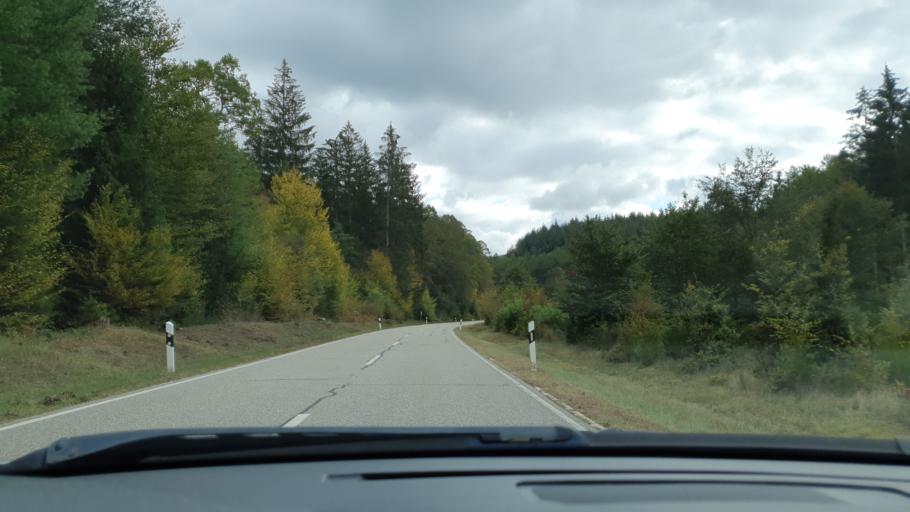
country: DE
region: Rheinland-Pfalz
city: Kaiserslautern
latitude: 49.4180
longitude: 7.8232
